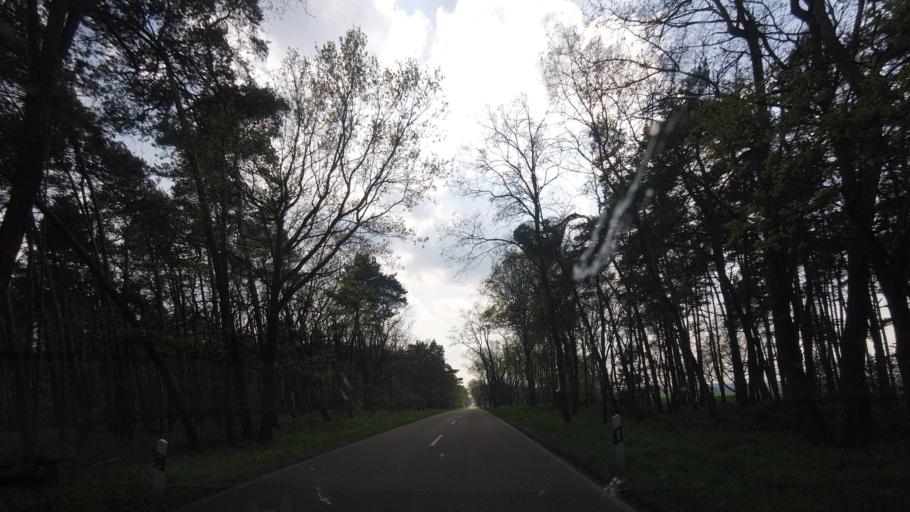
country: DE
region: Saxony-Anhalt
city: Zahna
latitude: 51.9296
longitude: 12.8262
